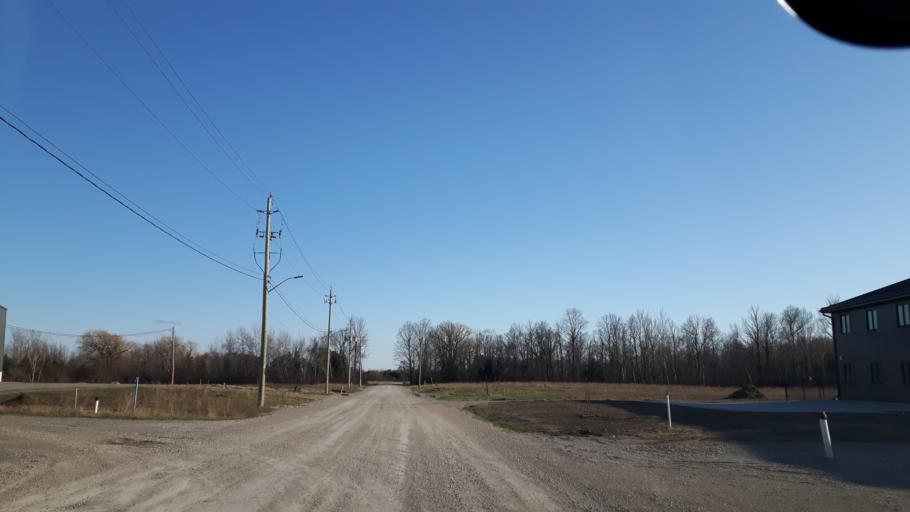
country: CA
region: Ontario
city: Goderich
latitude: 43.7277
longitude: -81.6938
